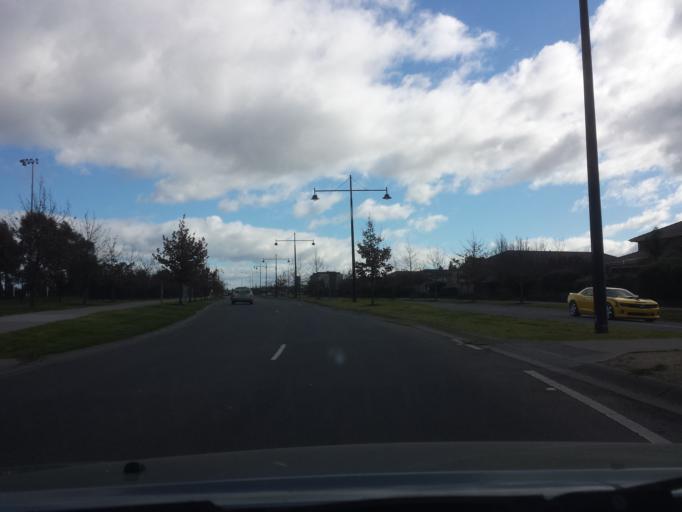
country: AU
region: Victoria
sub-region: Hume
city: Craigieburn
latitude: -37.5760
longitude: 144.9249
